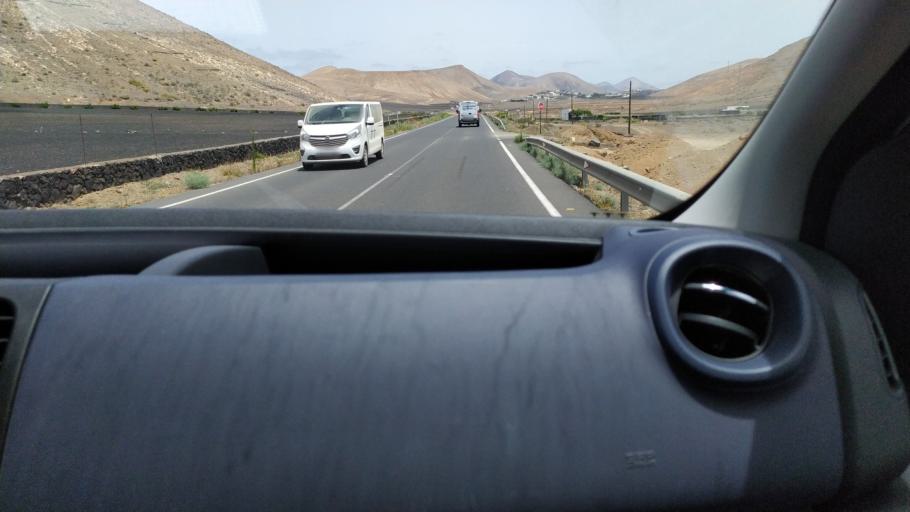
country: ES
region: Canary Islands
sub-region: Provincia de Las Palmas
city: Yaiza
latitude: 28.9198
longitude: -13.7707
